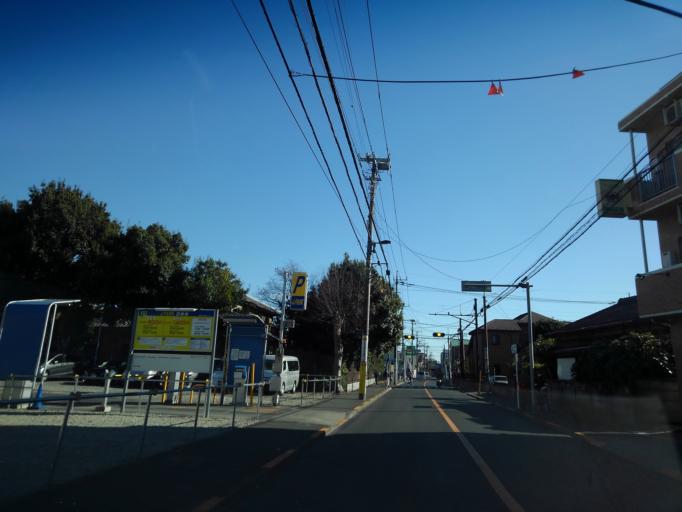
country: JP
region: Tokyo
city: Chofugaoka
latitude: 35.6635
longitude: 139.5203
